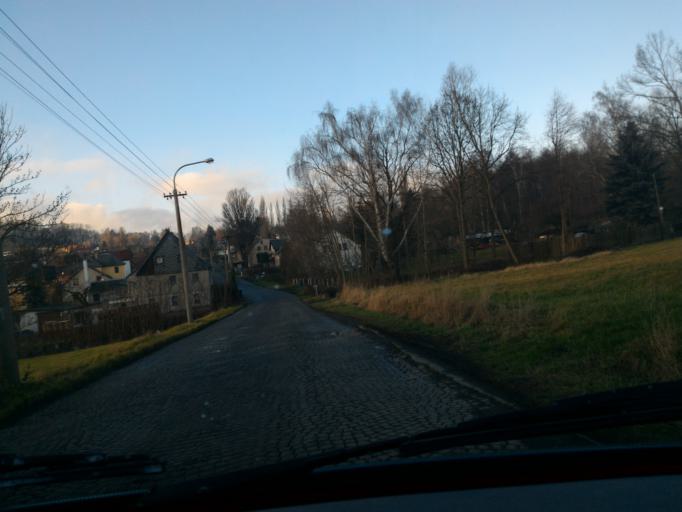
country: CZ
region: Ustecky
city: Varnsdorf
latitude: 50.9190
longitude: 14.6242
